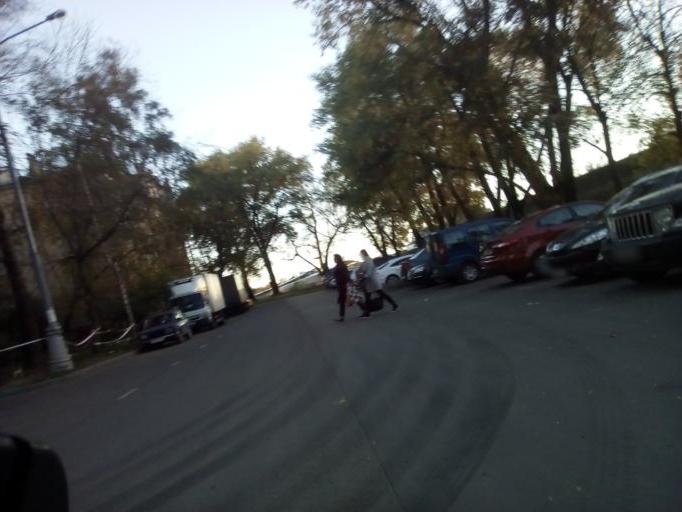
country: RU
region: Moskovskaya
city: Koptevo
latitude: 55.8168
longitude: 37.4874
